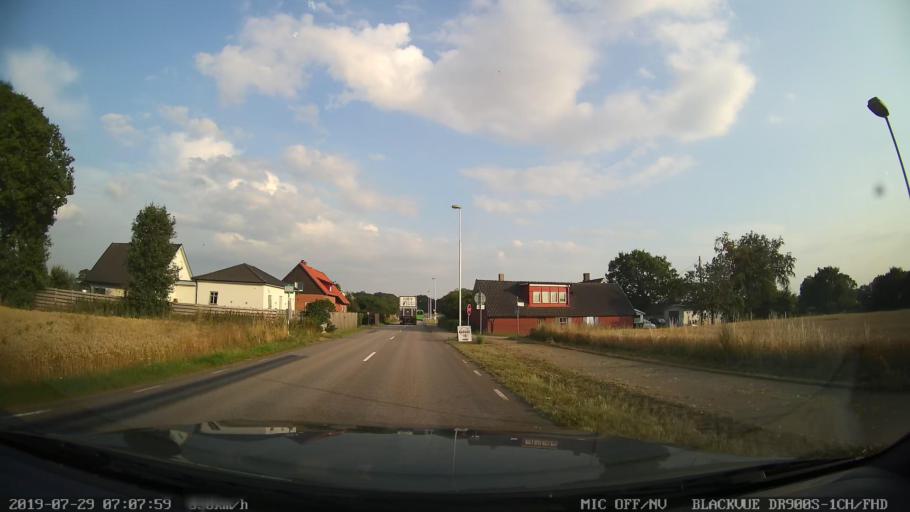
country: SE
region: Skane
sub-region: Helsingborg
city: Odakra
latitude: 56.1032
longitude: 12.6963
